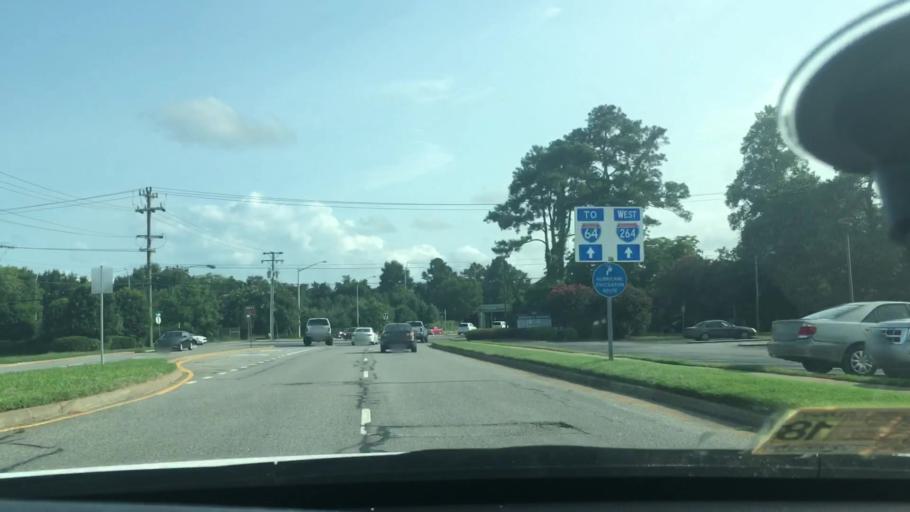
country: US
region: Virginia
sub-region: City of Virginia Beach
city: Virginia Beach
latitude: 36.8486
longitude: -75.9943
